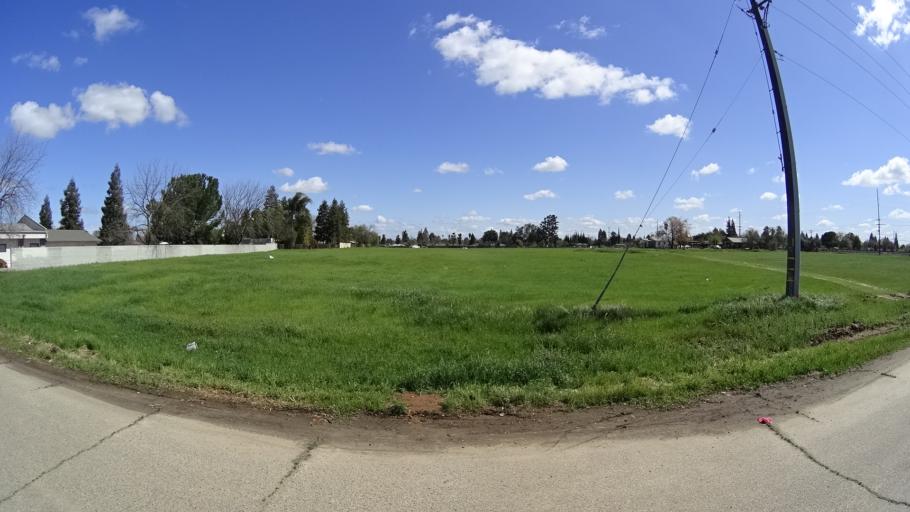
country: US
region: California
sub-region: Fresno County
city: West Park
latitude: 36.7951
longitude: -119.8896
